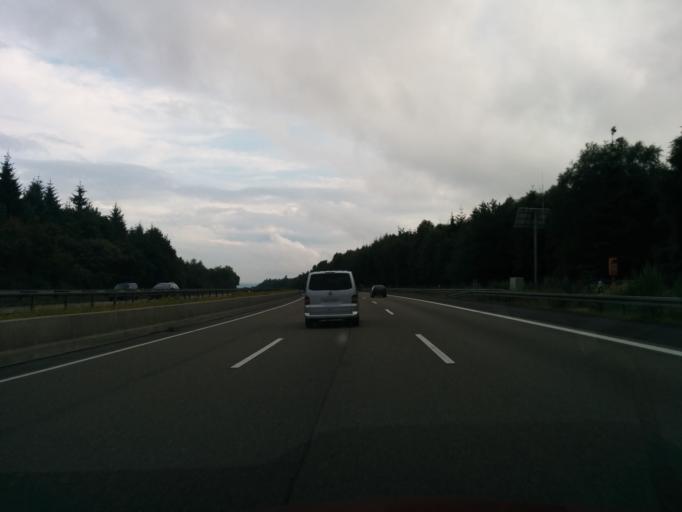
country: DE
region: Hesse
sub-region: Regierungsbezirk Kassel
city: Kirchheim
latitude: 50.8719
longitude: 9.5963
